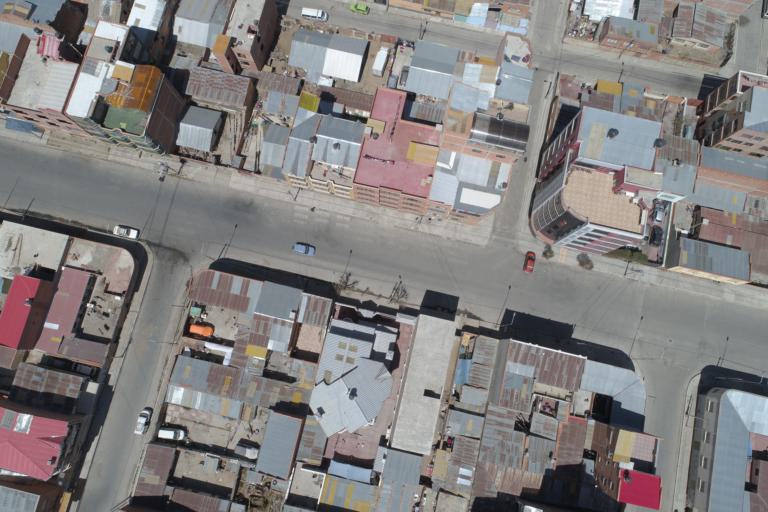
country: BO
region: La Paz
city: La Paz
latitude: -16.5193
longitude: -68.1531
